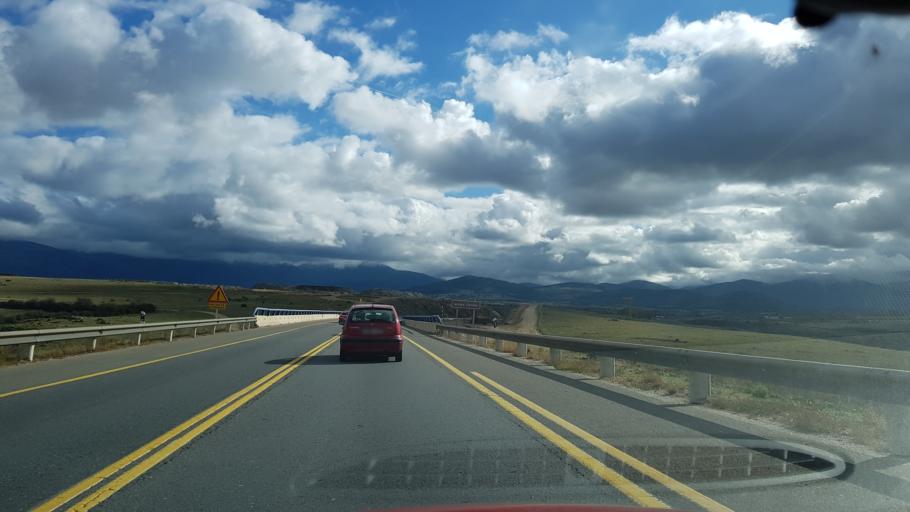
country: ES
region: Castille and Leon
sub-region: Provincia de Segovia
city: San Cristobal de Segovia
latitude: 40.9481
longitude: -4.0887
